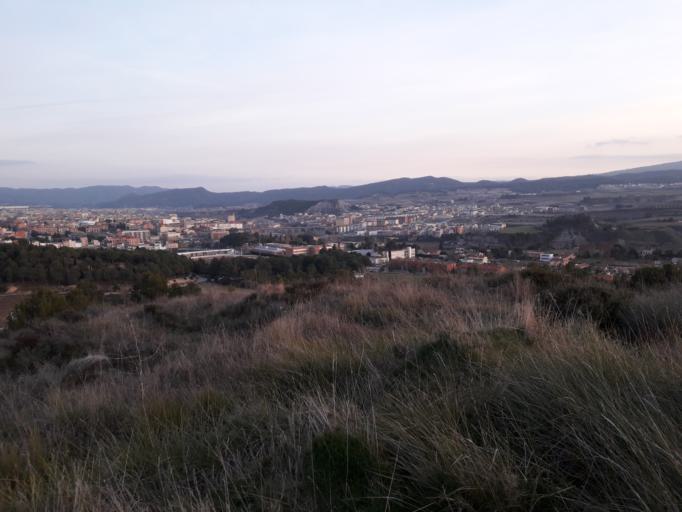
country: ES
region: Catalonia
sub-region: Provincia de Barcelona
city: Igualada
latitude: 41.5880
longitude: 1.5963
